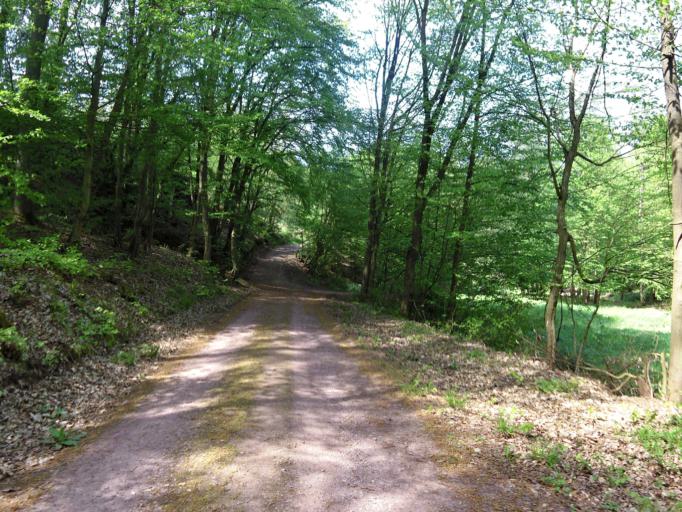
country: DE
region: Thuringia
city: Eisenach
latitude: 50.9665
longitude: 10.2973
